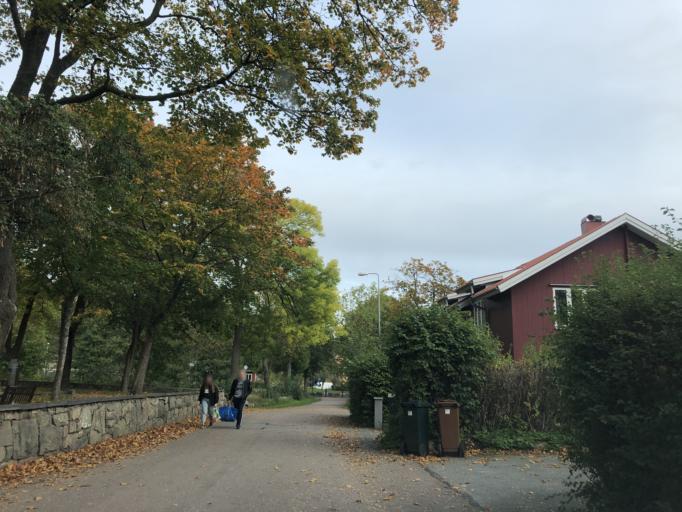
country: SE
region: Vaestra Goetaland
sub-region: Goteborg
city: Majorna
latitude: 57.6809
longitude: 11.8884
